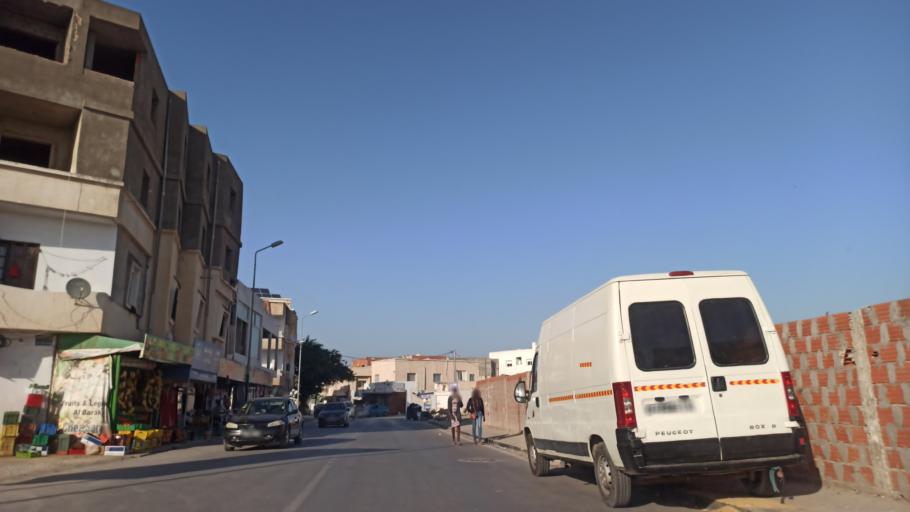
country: TN
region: Tunis
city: La Goulette
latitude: 36.8549
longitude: 10.2721
